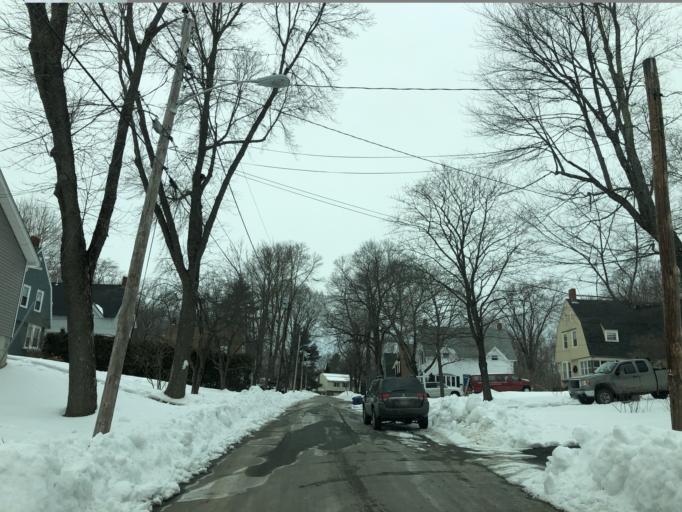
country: US
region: Maine
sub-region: Cumberland County
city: Westbrook
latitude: 43.6828
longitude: -70.3567
